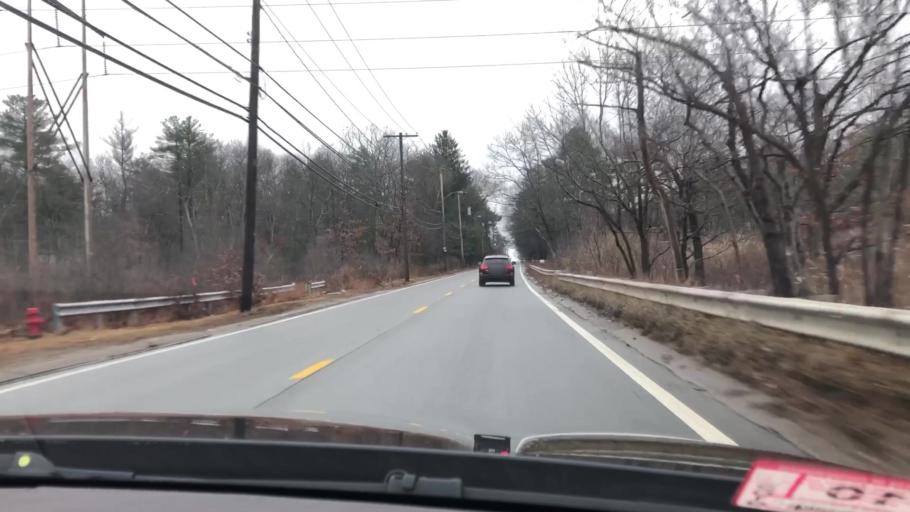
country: US
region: Massachusetts
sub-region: Norfolk County
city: Walpole
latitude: 42.1235
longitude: -71.2717
